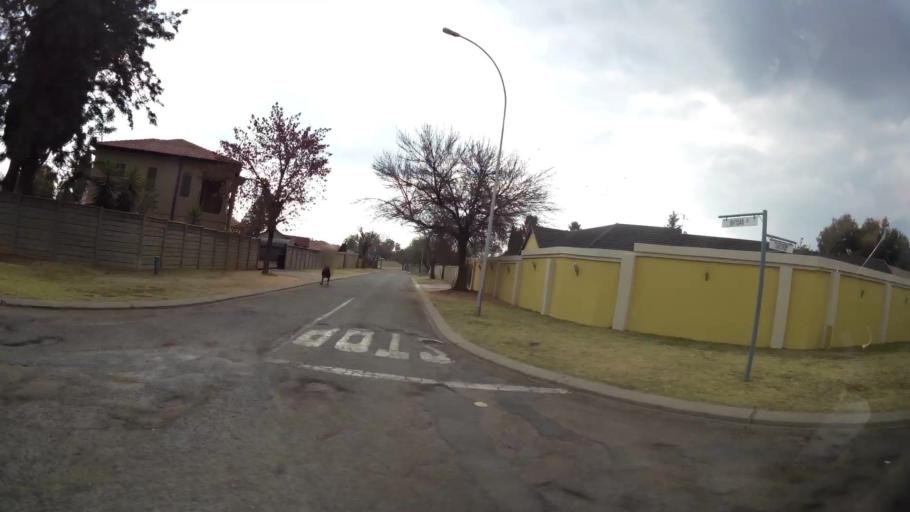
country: ZA
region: Gauteng
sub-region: Ekurhuleni Metropolitan Municipality
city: Benoni
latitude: -26.1162
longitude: 28.3723
